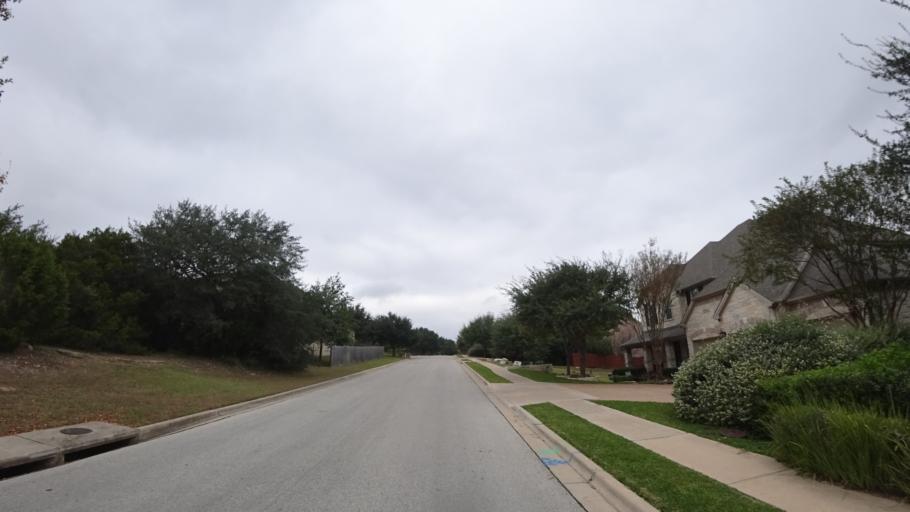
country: US
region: Texas
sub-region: Travis County
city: Hudson Bend
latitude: 30.3588
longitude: -97.9006
